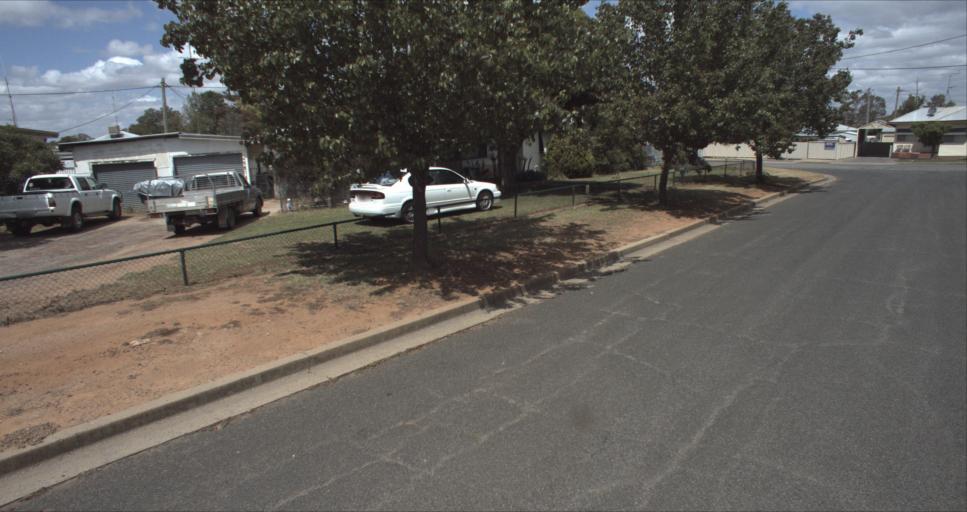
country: AU
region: New South Wales
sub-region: Leeton
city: Leeton
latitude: -34.5615
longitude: 146.3986
